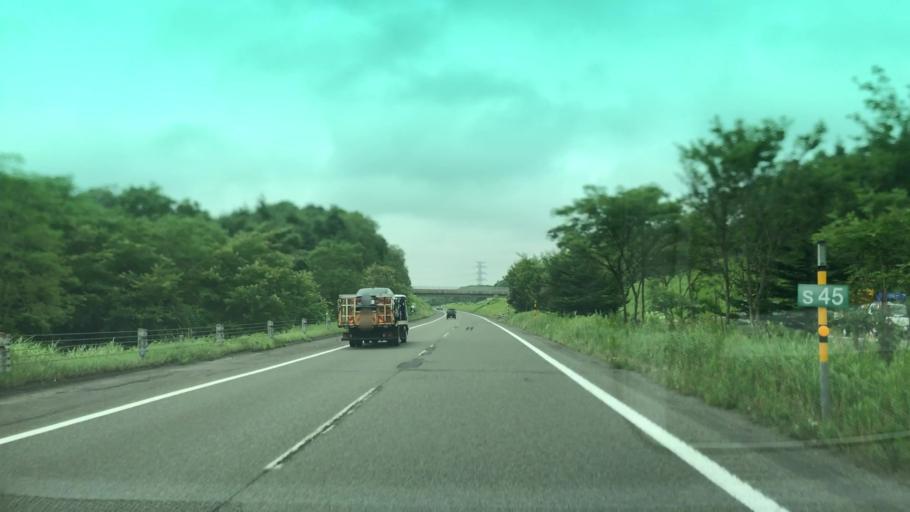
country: JP
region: Hokkaido
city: Chitose
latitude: 42.7296
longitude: 141.6530
